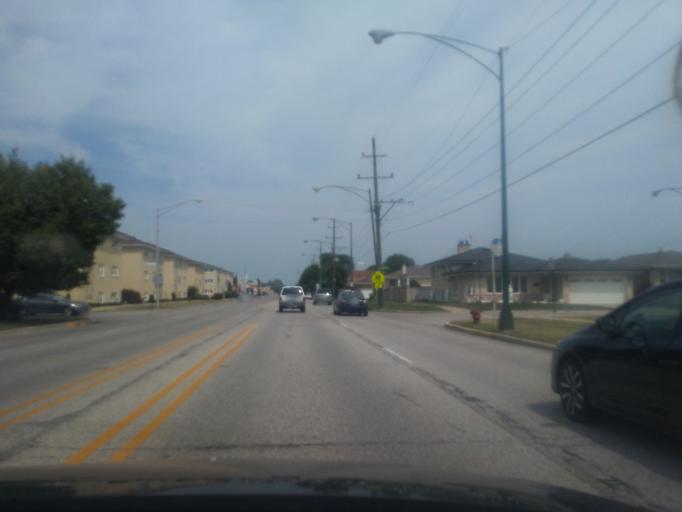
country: US
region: Illinois
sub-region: Cook County
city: Norridge
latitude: 41.9665
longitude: -87.8421
